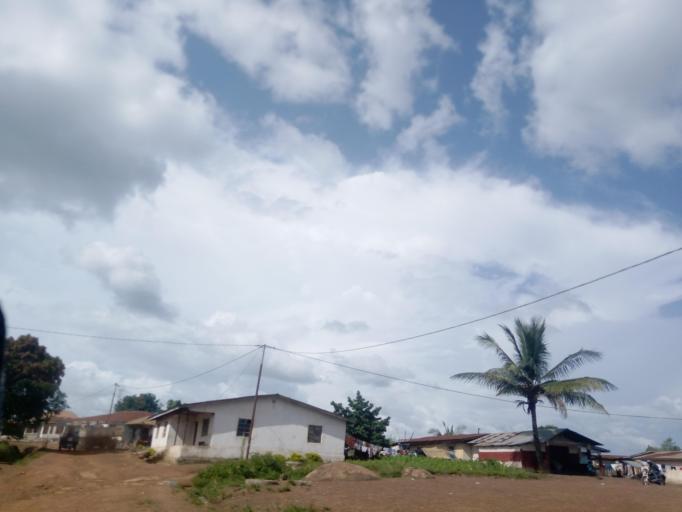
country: SL
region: Northern Province
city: Makeni
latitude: 8.9019
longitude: -12.0317
